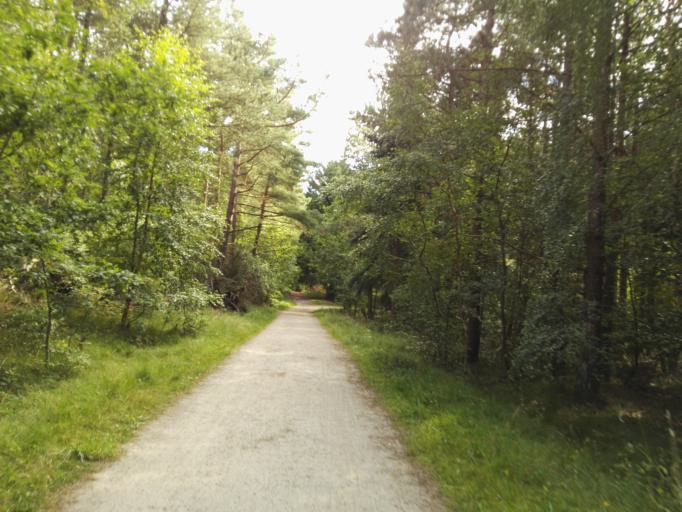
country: DK
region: Zealand
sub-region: Odsherred Kommune
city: Nykobing Sjaelland
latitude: 55.9454
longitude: 11.7031
